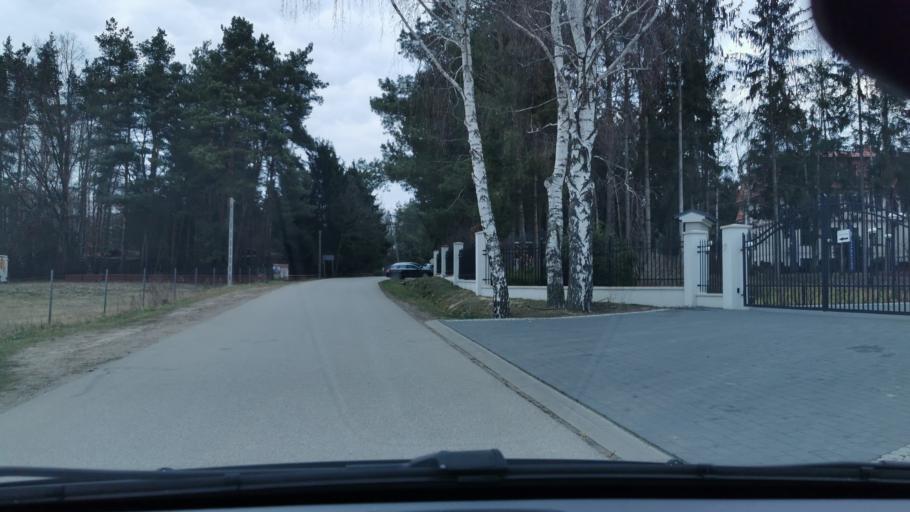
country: PL
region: Masovian Voivodeship
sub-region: Powiat zyrardowski
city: Radziejowice
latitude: 52.0122
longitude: 20.5210
